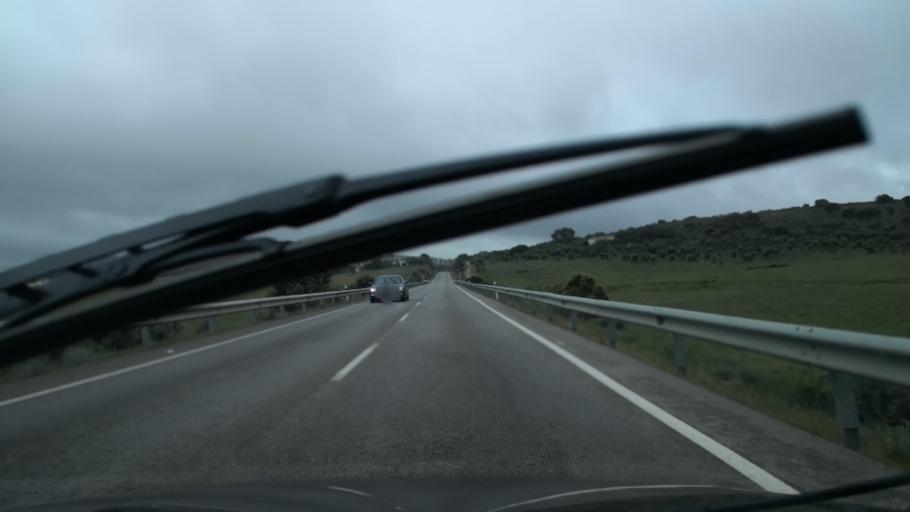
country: ES
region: Extremadura
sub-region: Provincia de Caceres
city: Caceres
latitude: 39.4927
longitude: -6.3849
